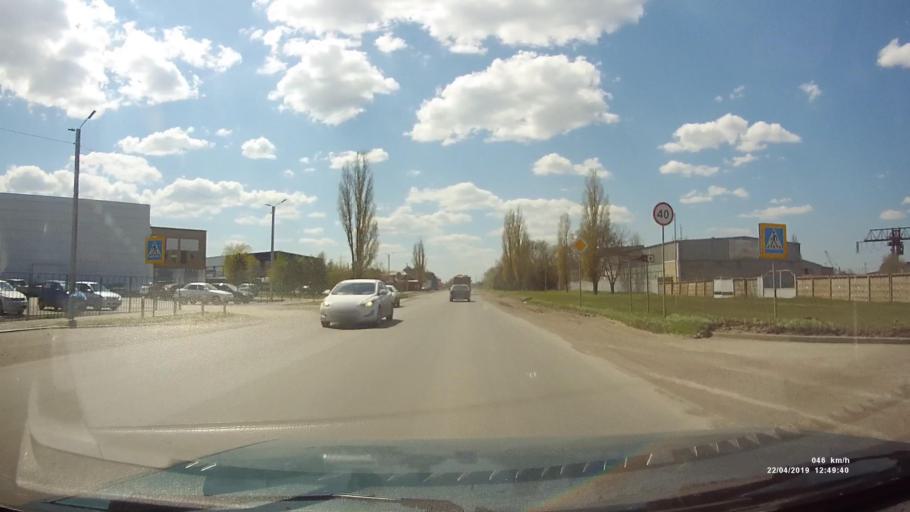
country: RU
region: Rostov
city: Azov
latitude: 47.0916
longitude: 39.3946
